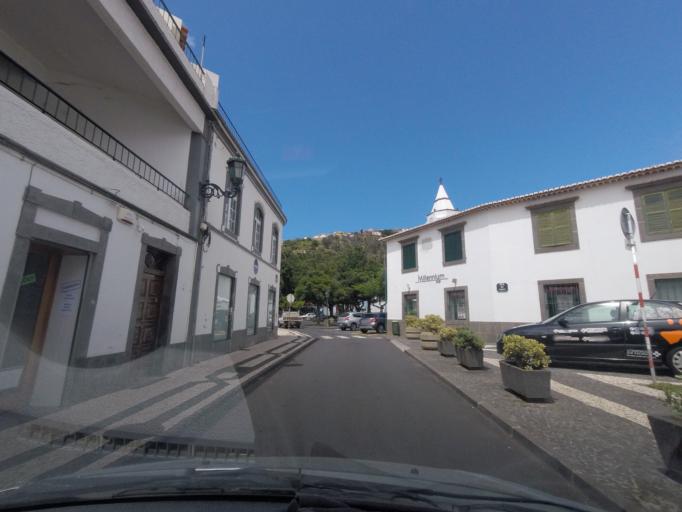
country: PT
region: Madeira
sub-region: Santa Cruz
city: Santa Cruz
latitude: 32.6883
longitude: -16.7916
